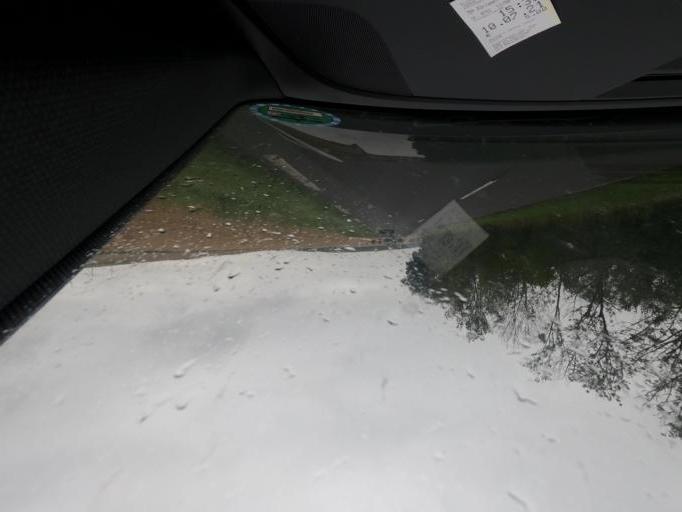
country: FR
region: Picardie
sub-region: Departement de la Somme
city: Moreuil
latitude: 49.8153
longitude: 2.4859
